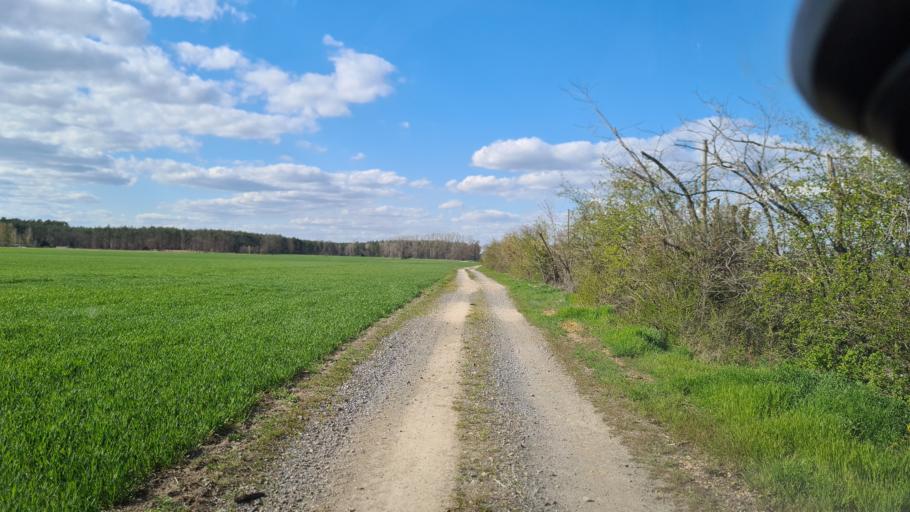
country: DE
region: Brandenburg
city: Falkenberg
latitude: 51.5209
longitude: 13.2724
